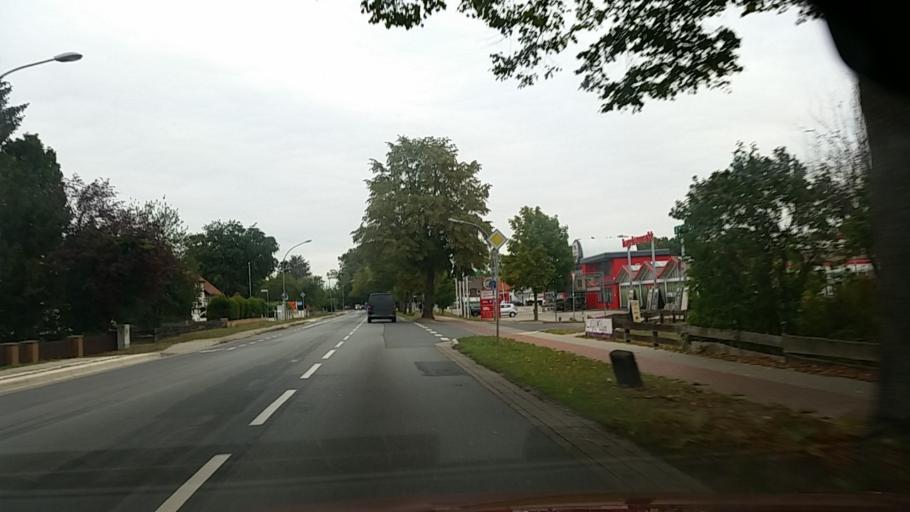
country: DE
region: Lower Saxony
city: Gifhorn
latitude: 52.4999
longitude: 10.5420
